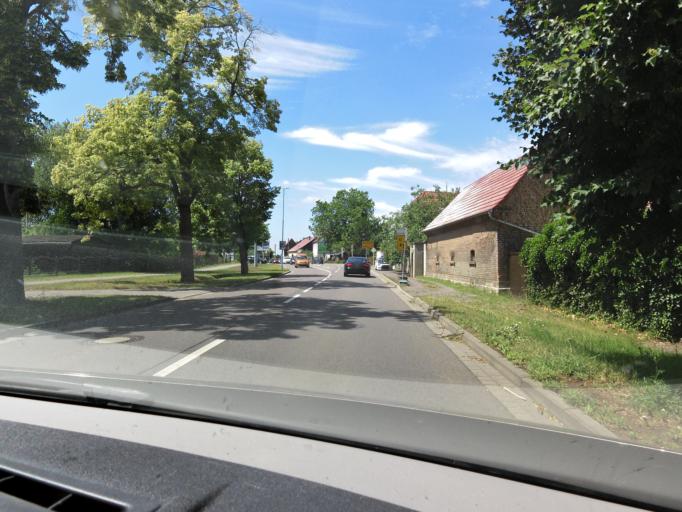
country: DE
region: Saxony-Anhalt
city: Wallendorf
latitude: 51.3593
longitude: 12.0747
